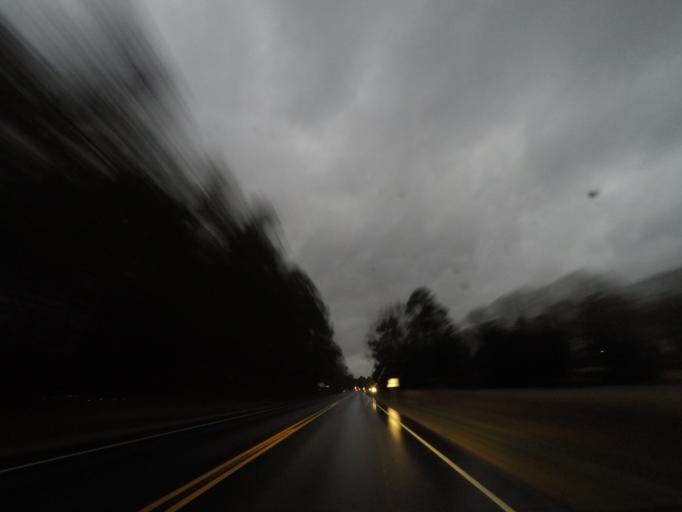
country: US
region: North Carolina
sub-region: Orange County
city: Hillsborough
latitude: 36.0768
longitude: -79.0724
